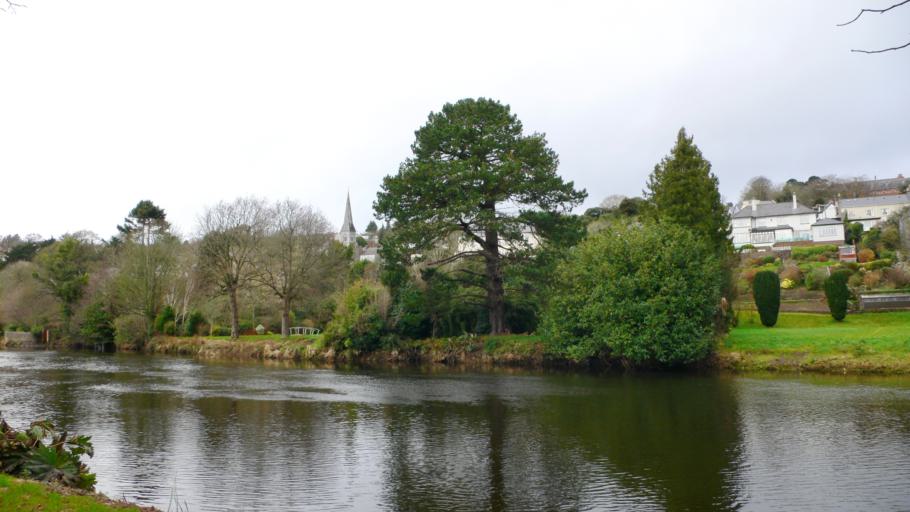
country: IE
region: Munster
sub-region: County Cork
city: Cork
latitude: 51.8965
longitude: -8.4961
